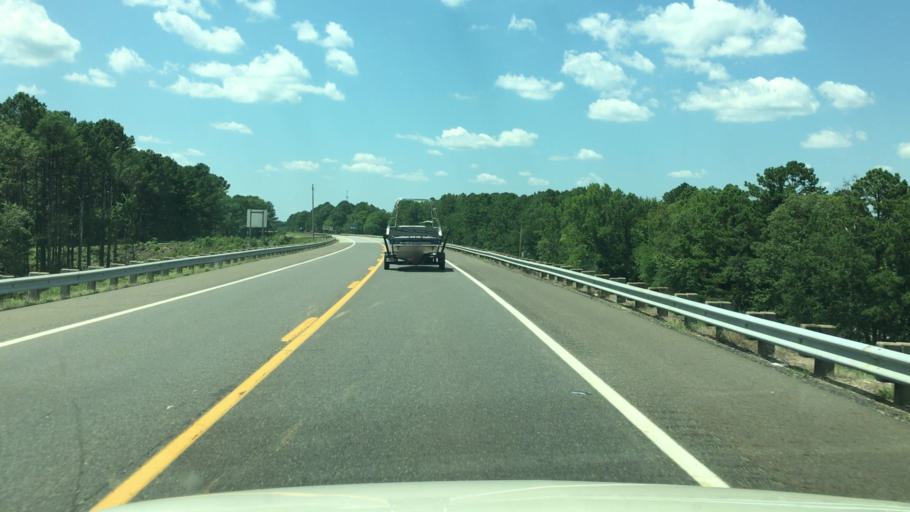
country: US
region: Arkansas
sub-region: Clark County
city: Arkadelphia
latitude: 34.2455
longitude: -93.1092
